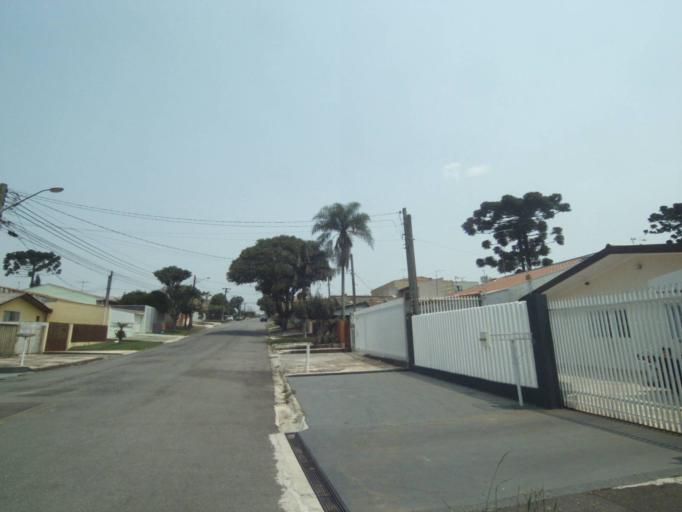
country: BR
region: Parana
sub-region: Sao Jose Dos Pinhais
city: Sao Jose dos Pinhais
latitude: -25.5257
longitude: -49.2454
